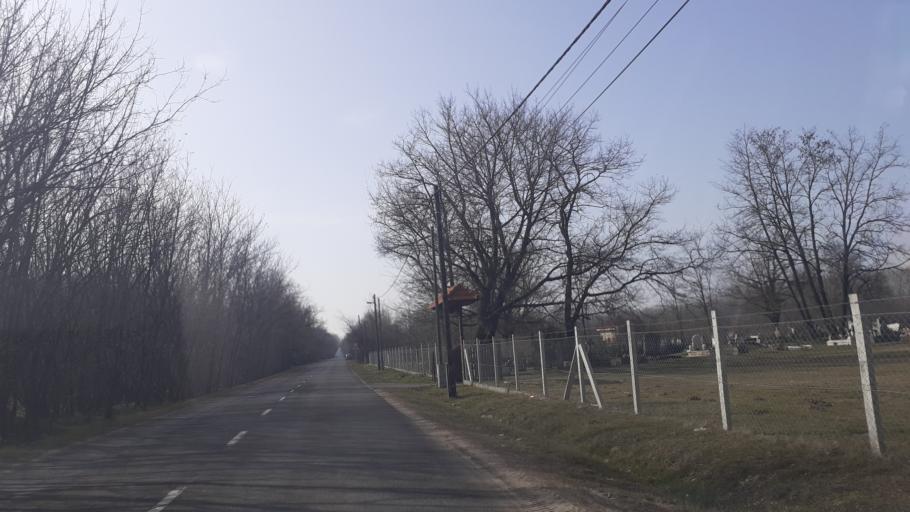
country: HU
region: Pest
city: Orkeny
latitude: 47.1224
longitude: 19.4195
